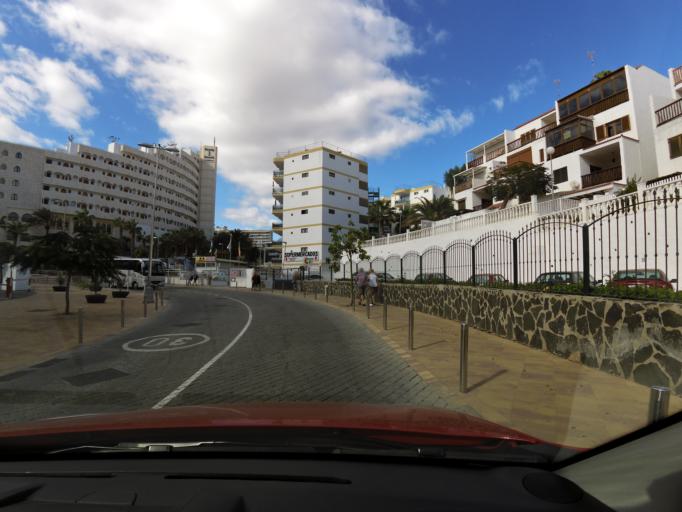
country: ES
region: Canary Islands
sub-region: Provincia de Las Palmas
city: Playa del Ingles
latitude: 27.7568
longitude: -15.5694
